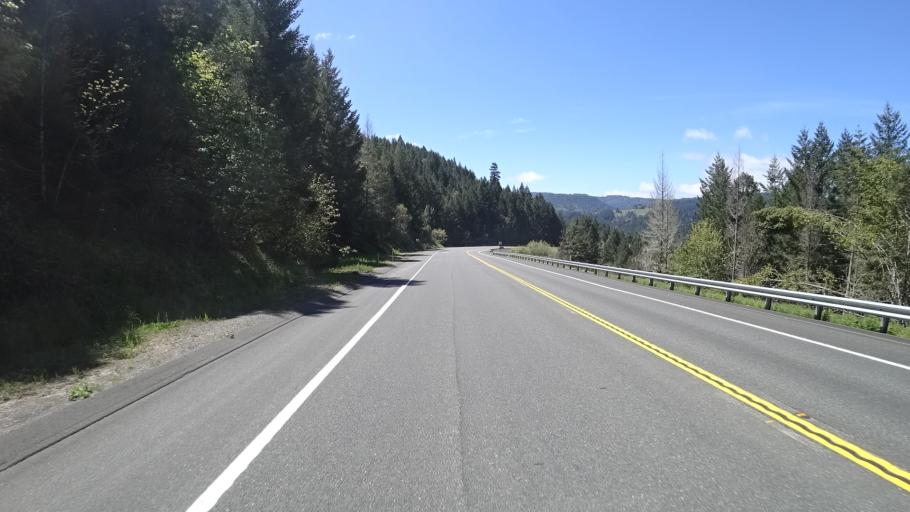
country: US
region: California
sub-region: Humboldt County
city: Willow Creek
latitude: 40.9159
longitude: -123.7995
